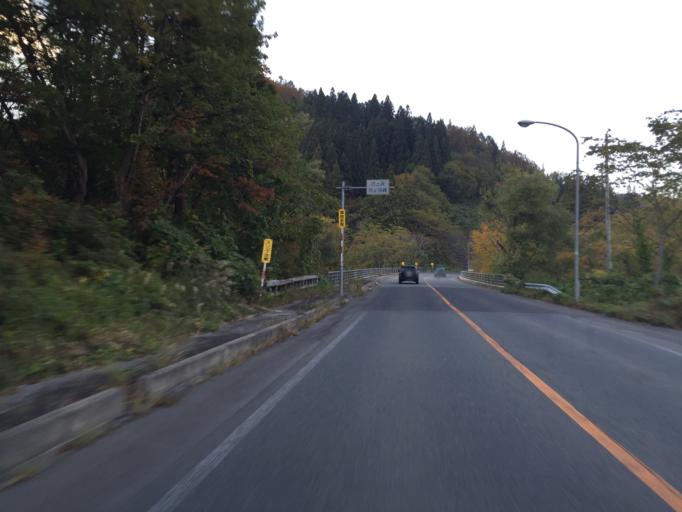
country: JP
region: Yamagata
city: Yonezawa
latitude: 37.8791
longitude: 139.9839
